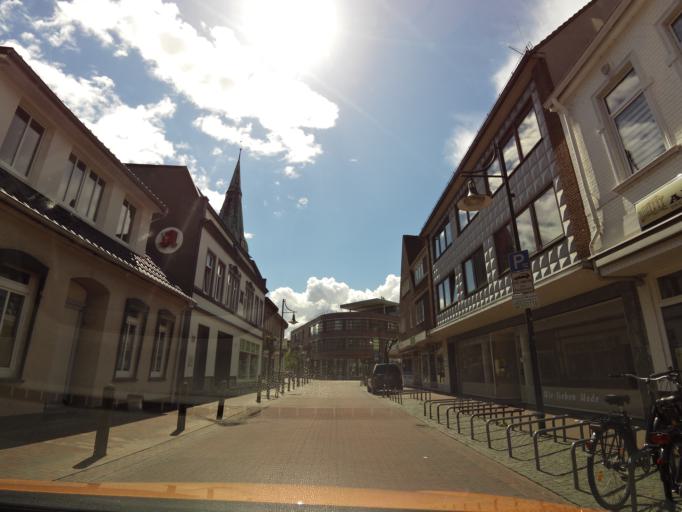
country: DE
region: Lower Saxony
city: Delmenhorst
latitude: 53.0507
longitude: 8.6301
